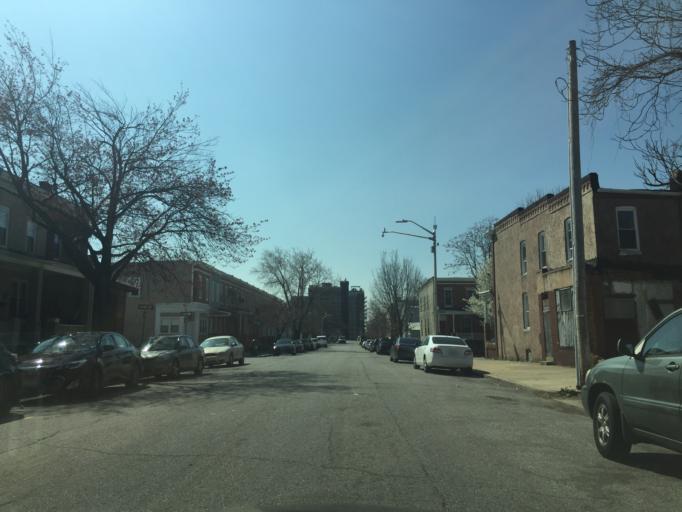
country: US
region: Maryland
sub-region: City of Baltimore
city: Baltimore
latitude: 39.3213
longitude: -76.6112
